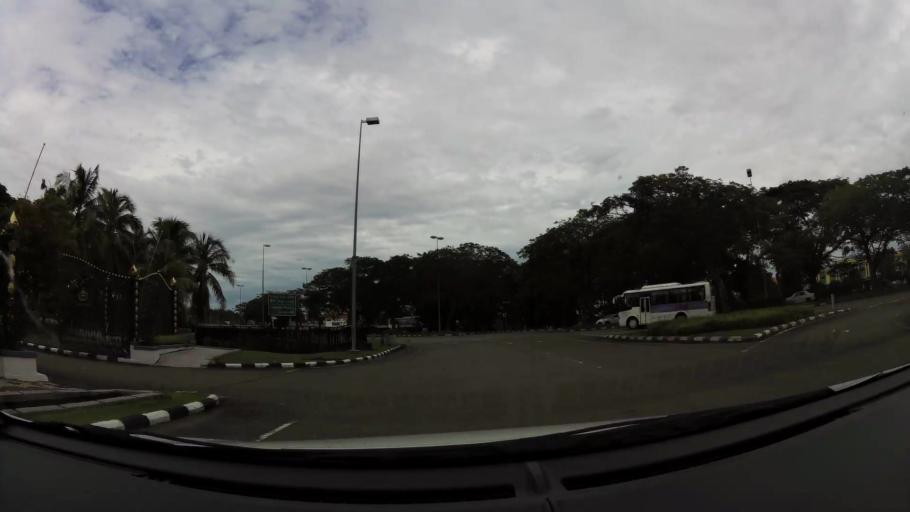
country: BN
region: Brunei and Muara
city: Bandar Seri Begawan
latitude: 4.8994
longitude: 114.9219
